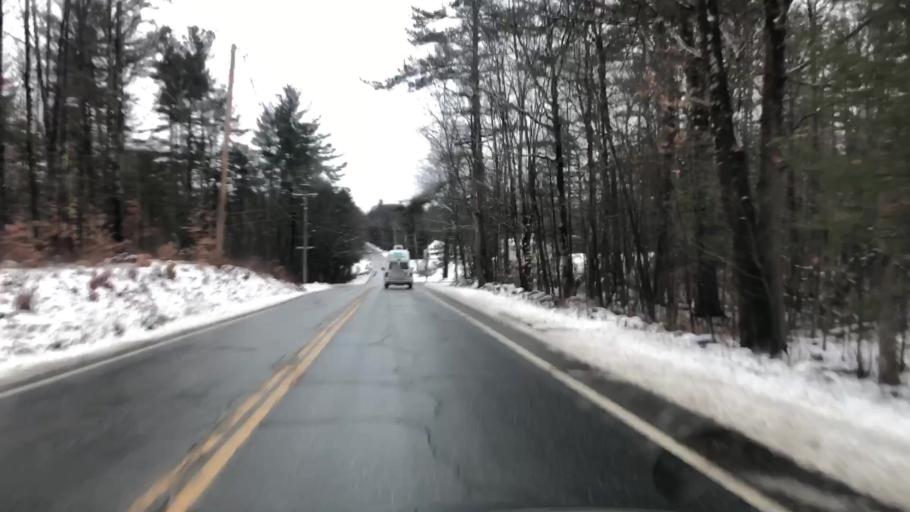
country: US
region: New Hampshire
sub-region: Hillsborough County
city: New Boston
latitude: 43.0177
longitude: -71.6895
